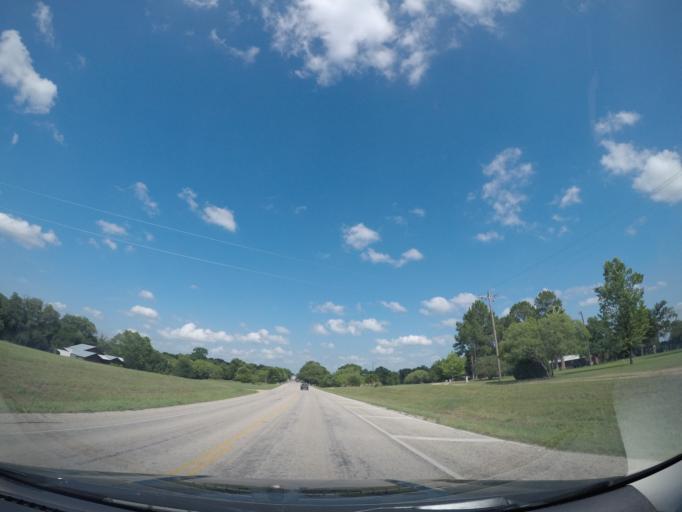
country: US
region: Texas
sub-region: Caldwell County
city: Luling
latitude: 29.5120
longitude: -97.6527
